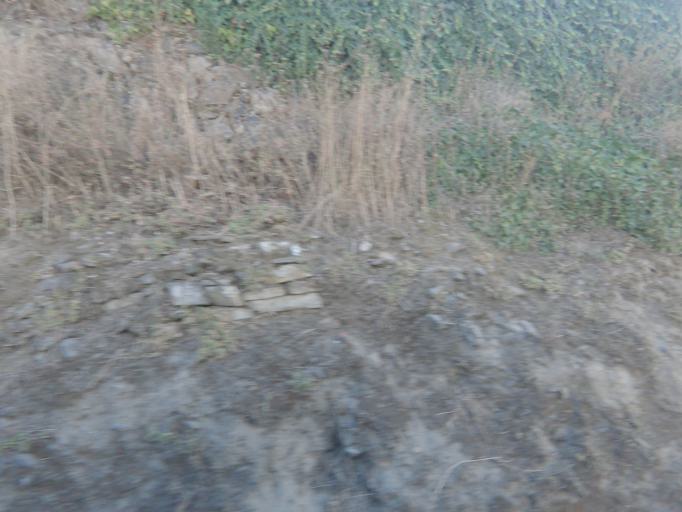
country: PT
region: Vila Real
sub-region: Peso da Regua
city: Peso da Regua
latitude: 41.1956
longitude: -7.7581
